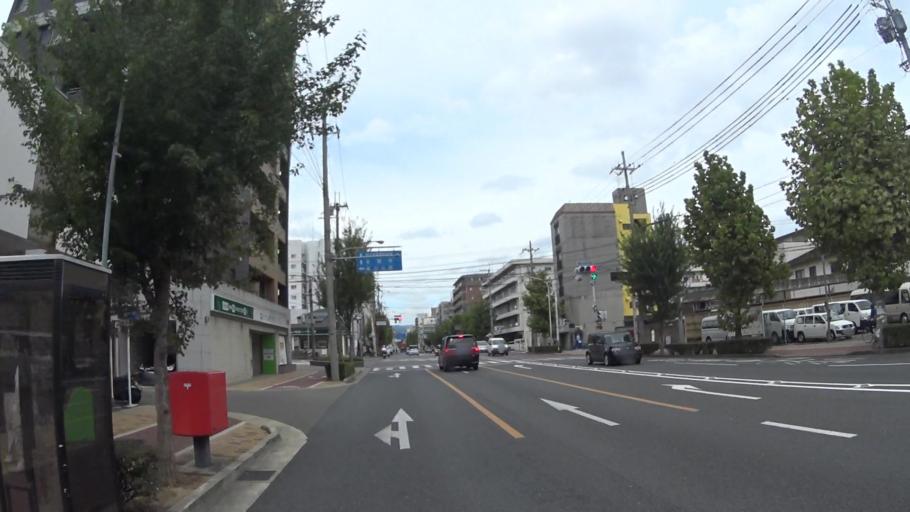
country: JP
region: Kyoto
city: Kyoto
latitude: 35.0076
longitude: 135.7318
